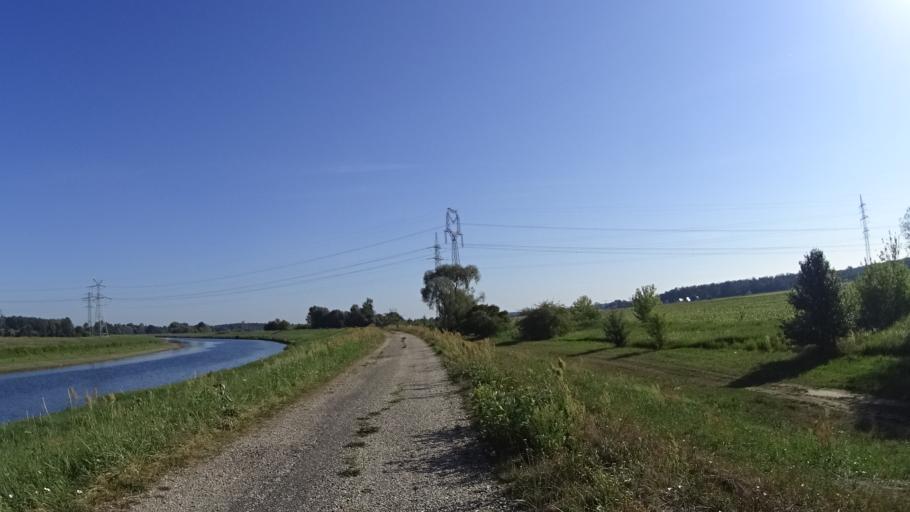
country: CZ
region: South Moravian
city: Kostice
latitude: 48.7171
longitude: 17.0123
